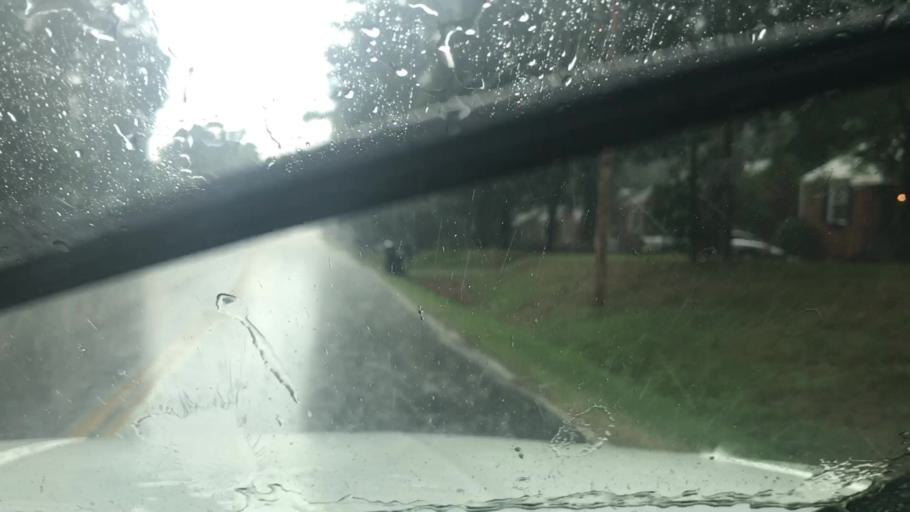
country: US
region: Virginia
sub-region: Henrico County
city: Tuckahoe
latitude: 37.6021
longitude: -77.5377
